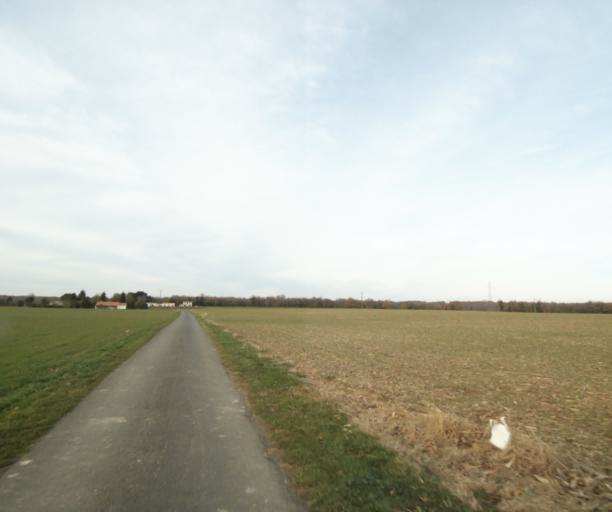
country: FR
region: Poitou-Charentes
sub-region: Departement de la Charente-Maritime
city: Saint-Hilaire-de-Villefranche
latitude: 45.8331
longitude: -0.5807
